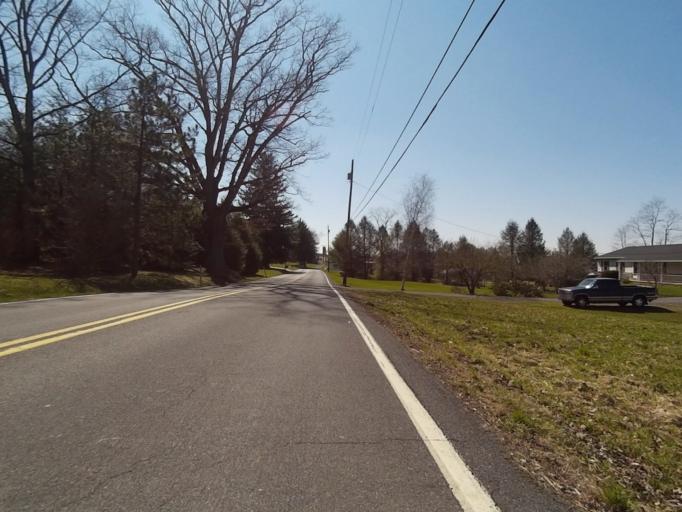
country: US
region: Pennsylvania
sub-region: Centre County
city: Stormstown
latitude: 40.7458
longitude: -78.0037
